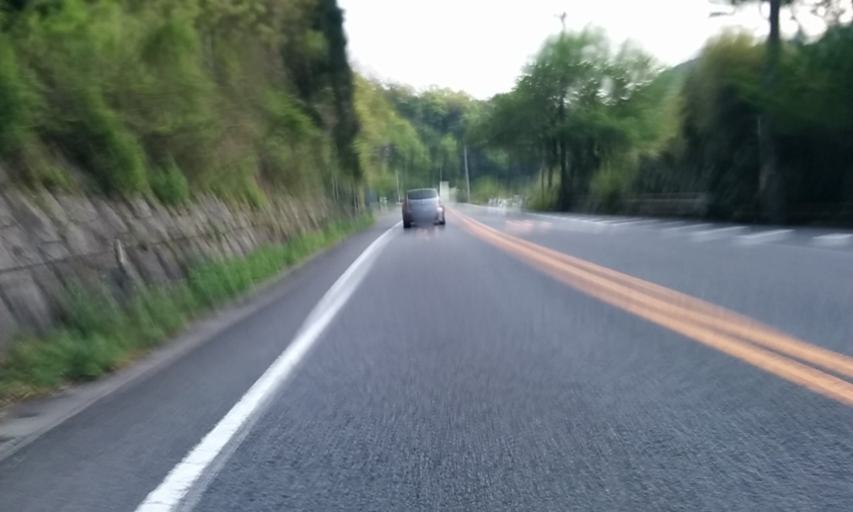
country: JP
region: Ehime
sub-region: Shikoku-chuo Shi
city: Matsuyama
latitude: 33.8163
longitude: 132.9807
